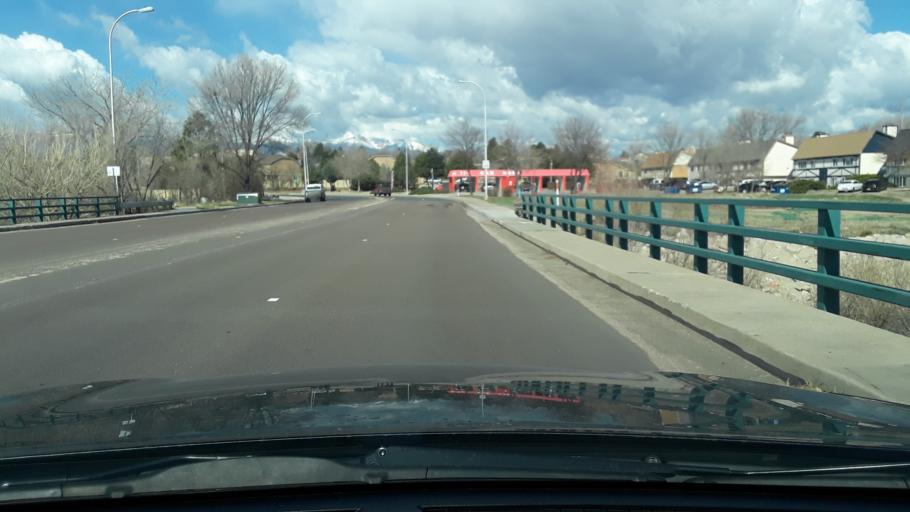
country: US
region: Colorado
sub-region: El Paso County
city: Cimarron Hills
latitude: 38.8572
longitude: -104.7239
